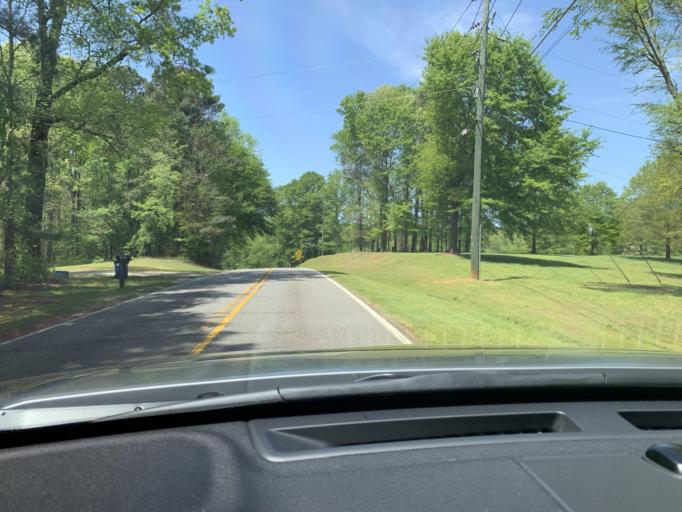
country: US
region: Georgia
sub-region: Barrow County
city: Statham
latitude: 33.9018
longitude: -83.6132
